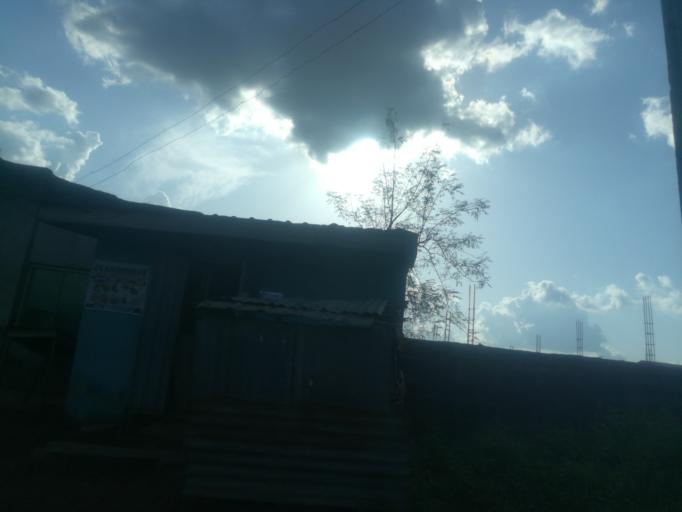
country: NG
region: Oyo
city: Lalupon
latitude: 7.4381
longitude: 3.9820
